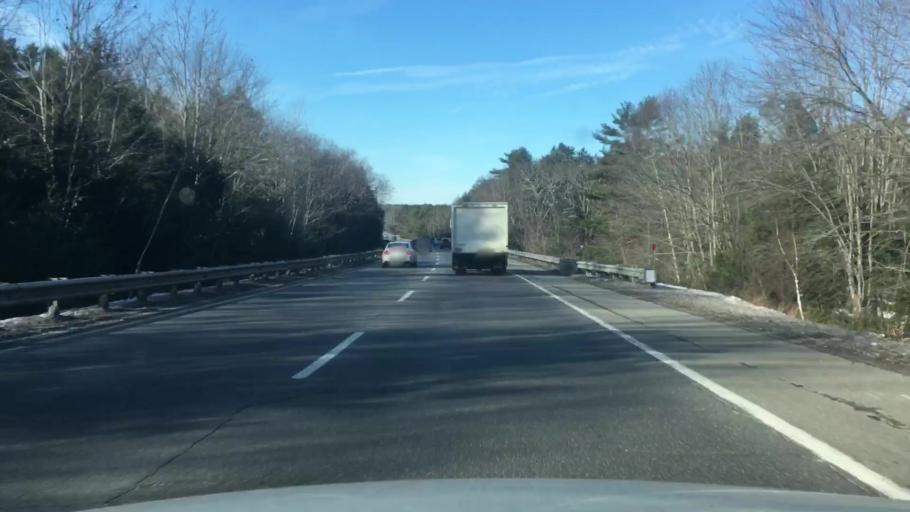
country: US
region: Maine
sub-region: Sagadahoc County
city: Bath
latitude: 43.9145
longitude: -69.8493
